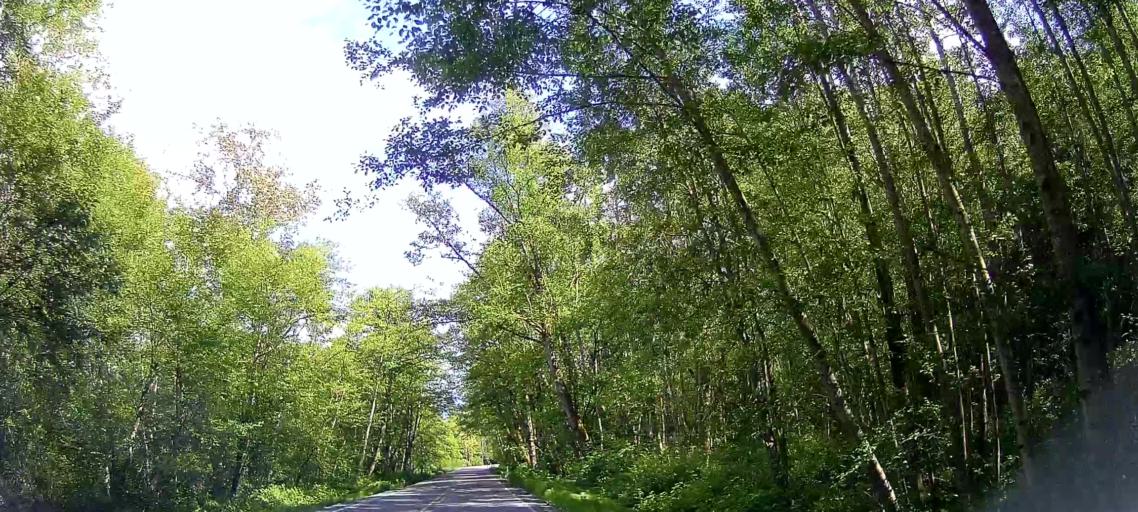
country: US
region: Washington
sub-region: Skagit County
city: Sedro-Woolley
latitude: 48.5326
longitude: -122.2200
